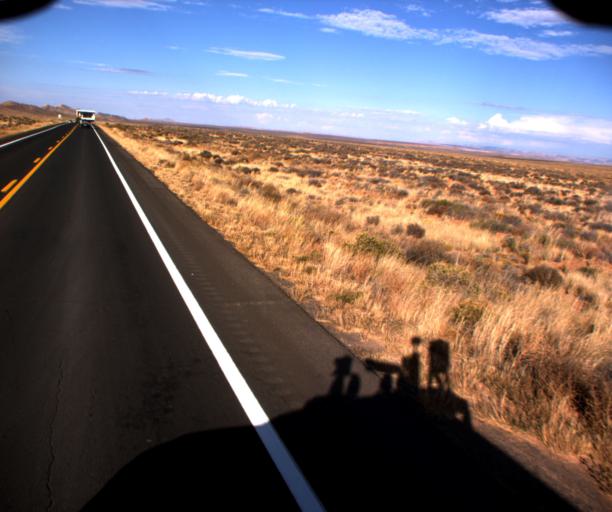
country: US
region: Arizona
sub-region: Apache County
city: Lukachukai
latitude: 36.9633
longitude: -109.4560
